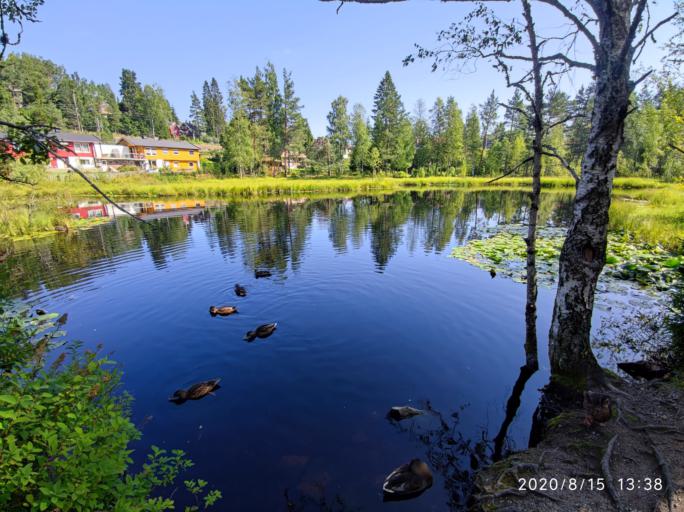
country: NO
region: Akershus
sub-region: Nittedal
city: Rotnes
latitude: 60.0587
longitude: 10.8567
